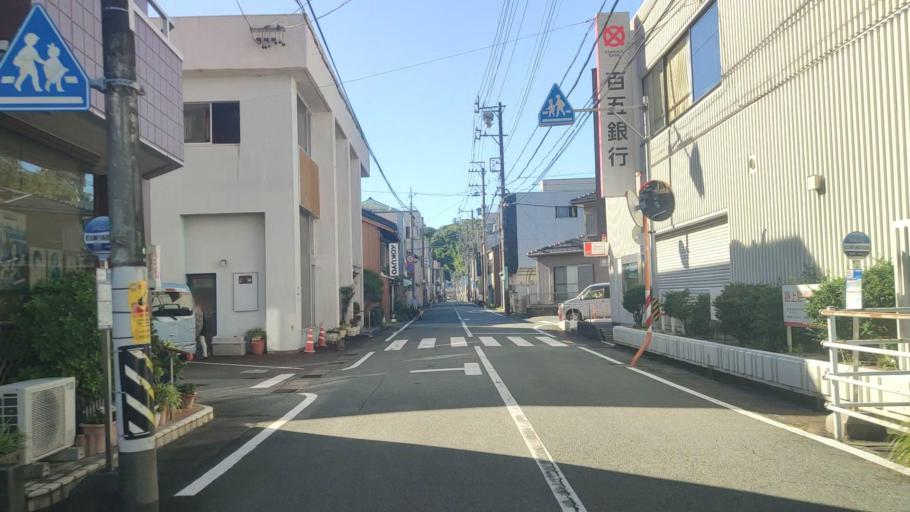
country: JP
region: Mie
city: Toba
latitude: 34.4796
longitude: 136.8440
